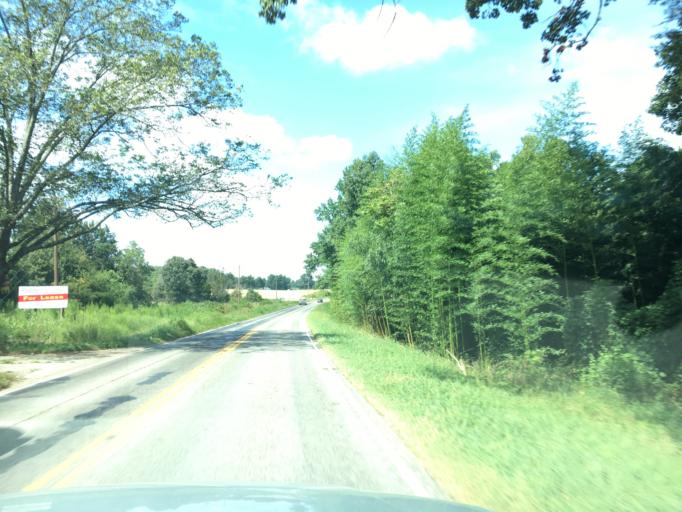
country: US
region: South Carolina
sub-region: Spartanburg County
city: Inman Mills
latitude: 35.0112
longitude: -82.1102
